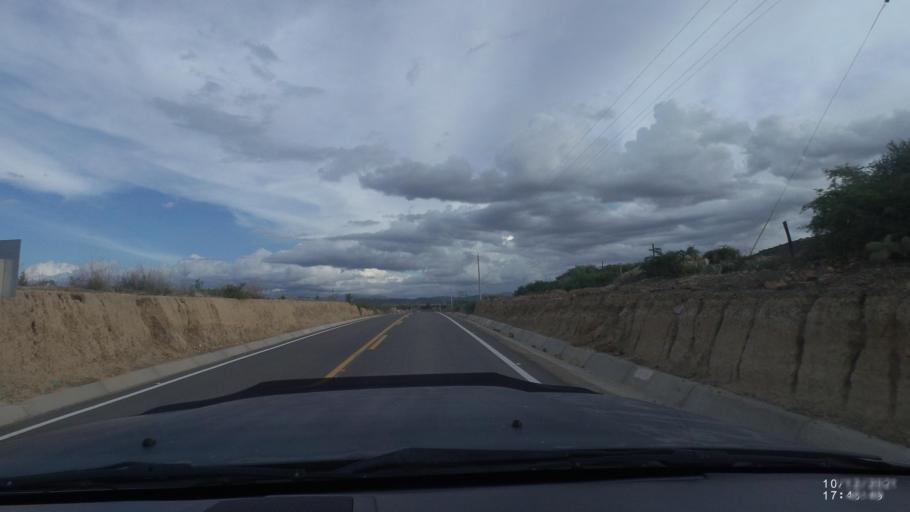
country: BO
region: Cochabamba
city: Tarata
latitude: -17.6336
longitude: -65.9909
